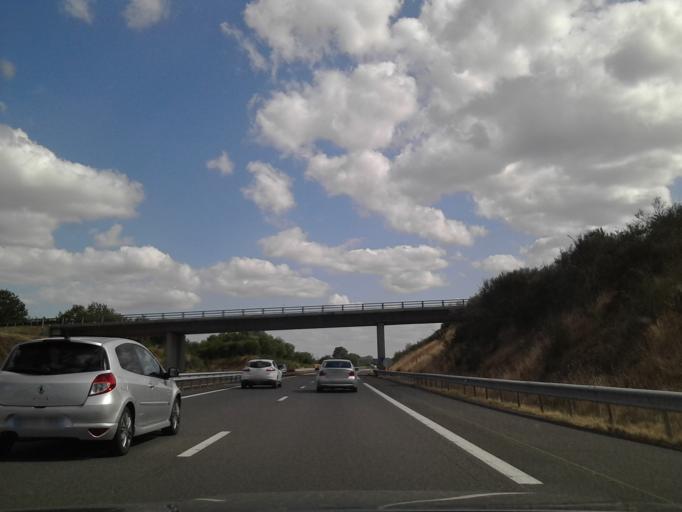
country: FR
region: Auvergne
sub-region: Departement de l'Allier
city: Estivareilles
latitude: 46.3981
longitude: 2.7144
